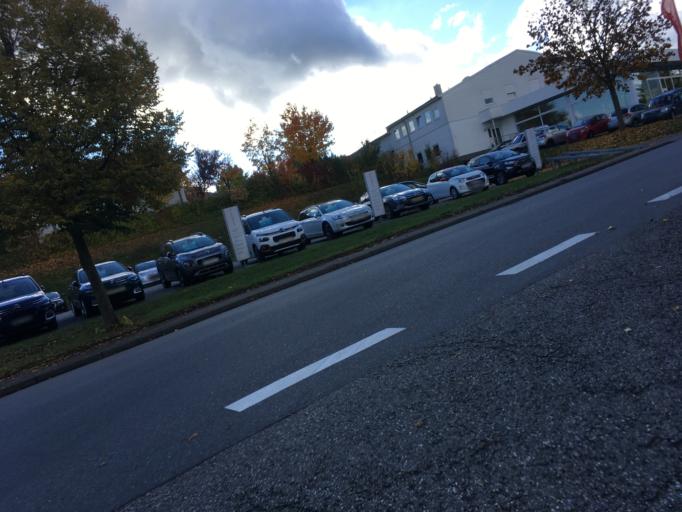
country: DE
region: Baden-Wuerttemberg
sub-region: Regierungsbezirk Stuttgart
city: Ohringen
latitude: 49.1943
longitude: 9.4850
